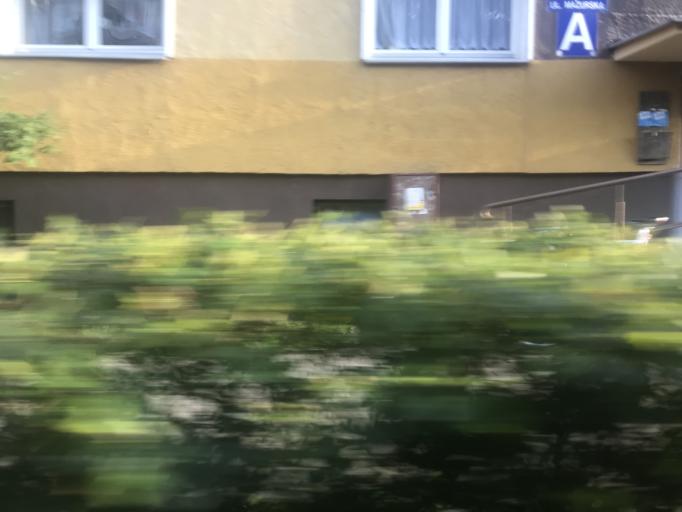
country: PL
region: Pomeranian Voivodeship
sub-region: Gdansk
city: Gdansk
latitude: 54.4083
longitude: 18.6333
